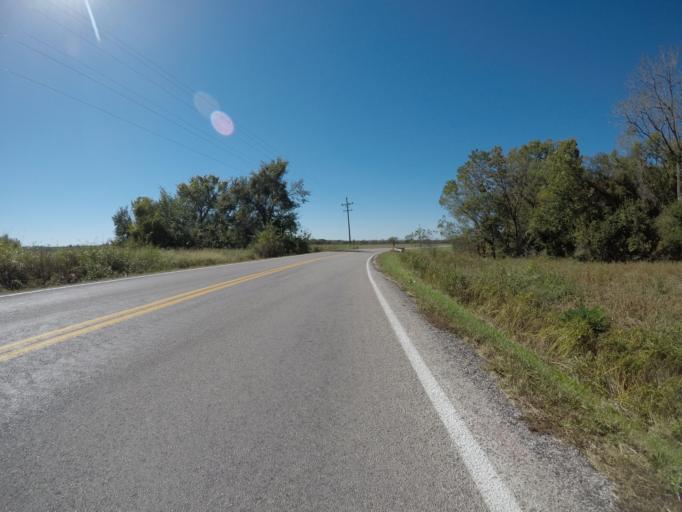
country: US
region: Kansas
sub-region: Johnson County
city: De Soto
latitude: 38.9995
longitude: -94.9511
